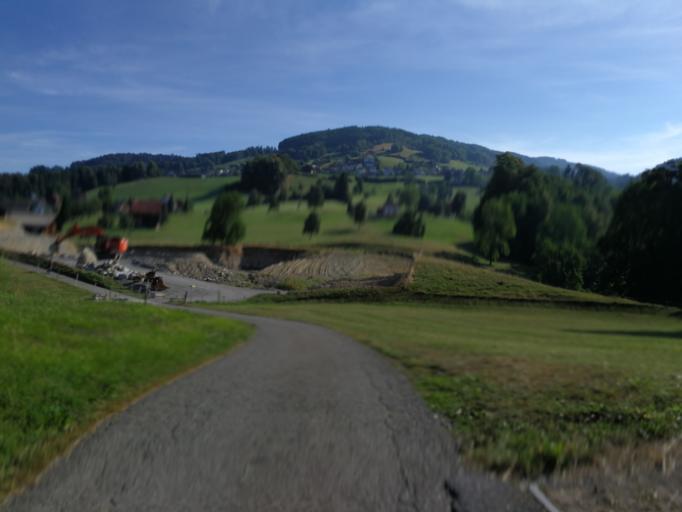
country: CH
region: Saint Gallen
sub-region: Wahlkreis See-Gaster
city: Gommiswald
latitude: 47.2252
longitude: 9.0292
